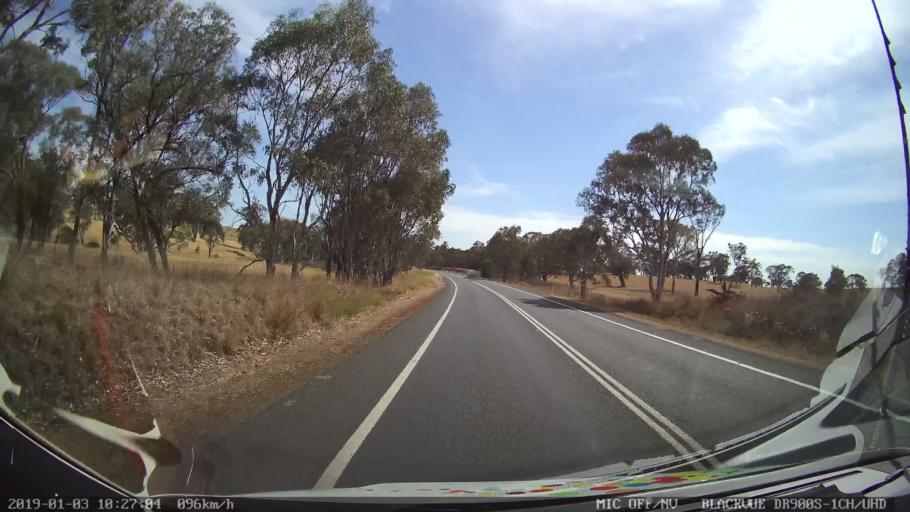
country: AU
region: New South Wales
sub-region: Young
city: Young
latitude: -34.4068
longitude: 148.2565
